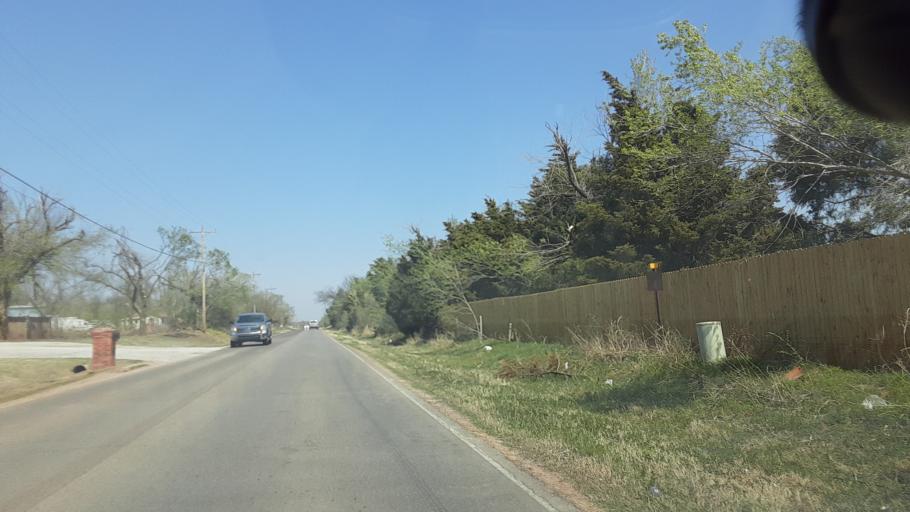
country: US
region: Oklahoma
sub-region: Oklahoma County
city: Edmond
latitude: 35.7298
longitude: -97.4784
